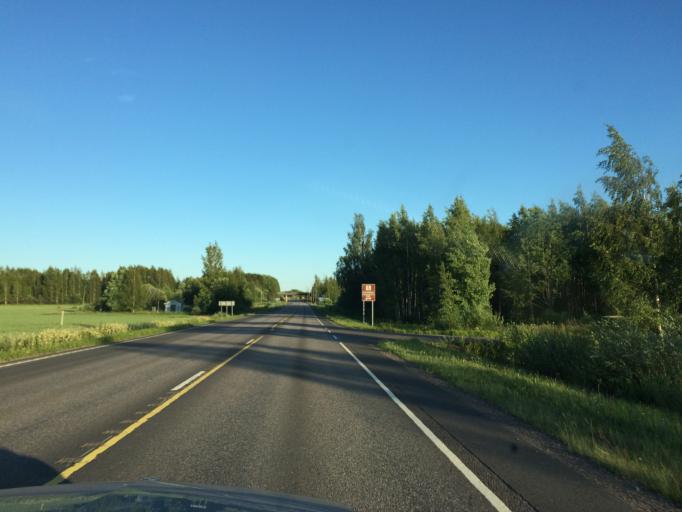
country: FI
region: Haeme
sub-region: Haemeenlinna
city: Tervakoski
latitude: 60.8218
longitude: 24.6367
